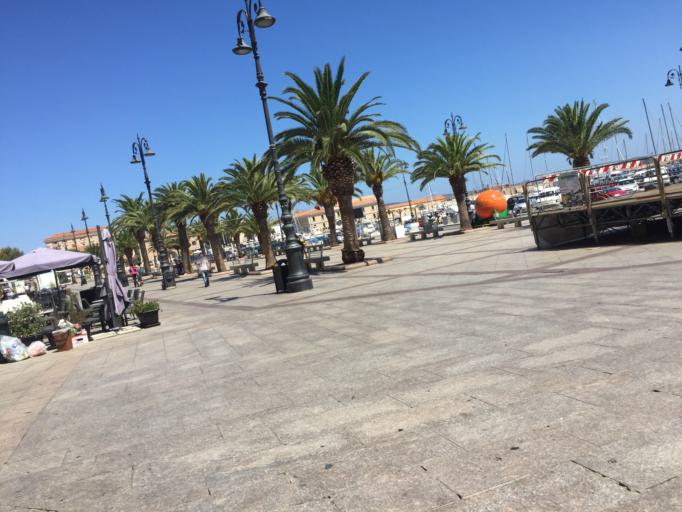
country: IT
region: Sardinia
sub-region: Provincia di Olbia-Tempio
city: La Maddalena
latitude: 41.2145
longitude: 9.4084
